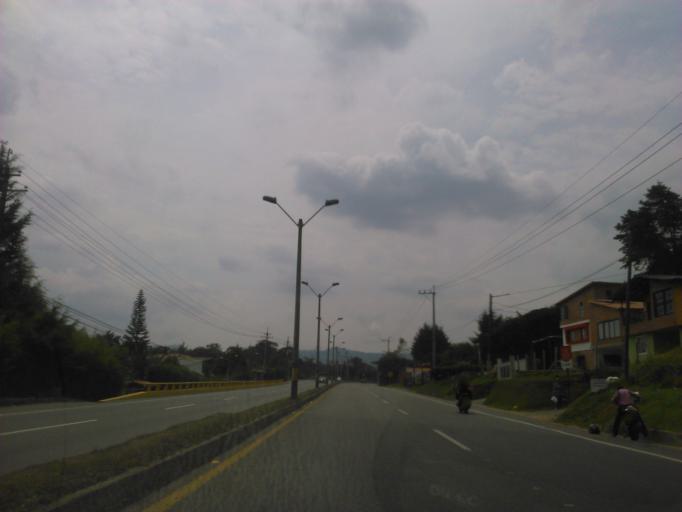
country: CO
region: Antioquia
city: Guarne
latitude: 6.2292
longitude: -75.4060
